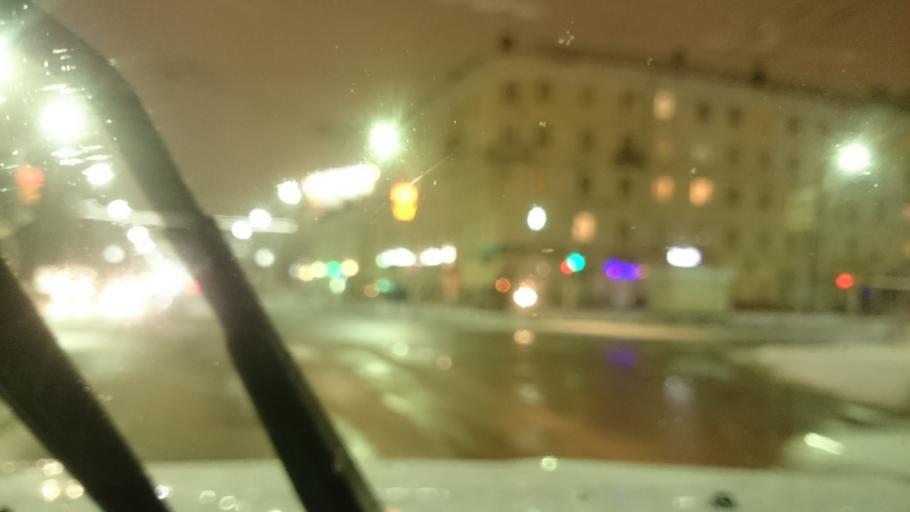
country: RU
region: Tula
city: Tula
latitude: 54.1985
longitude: 37.5848
